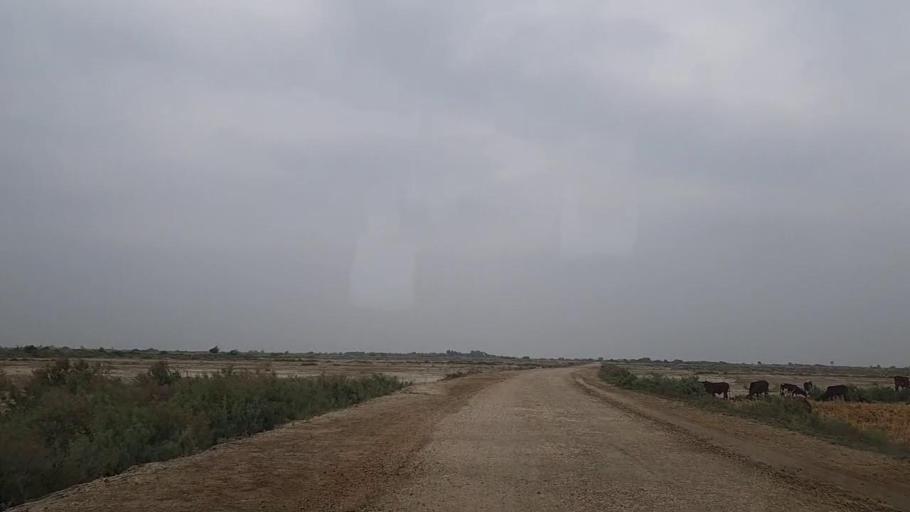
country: PK
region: Sindh
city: Mirpur Sakro
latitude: 24.6294
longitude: 67.7190
